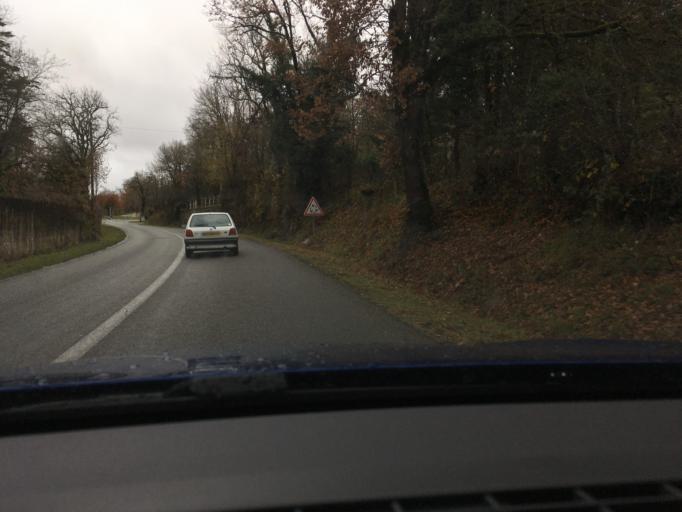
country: FR
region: Midi-Pyrenees
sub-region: Departement de l'Aveyron
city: Villefranche-de-Rouergue
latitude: 44.3757
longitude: 2.0123
